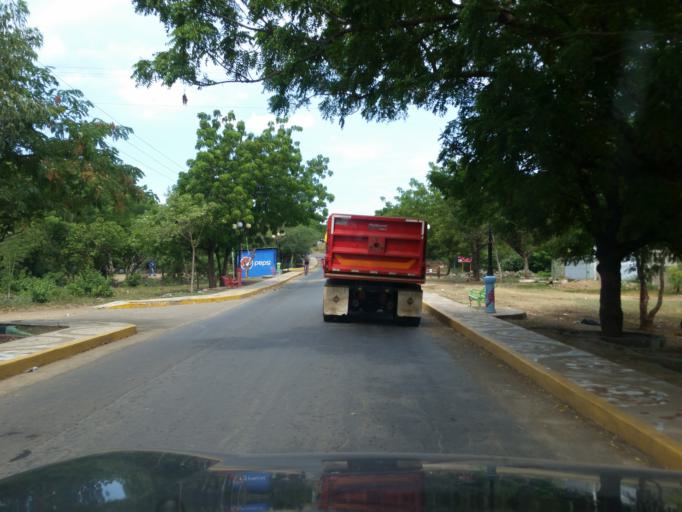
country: NI
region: Managua
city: Masachapa
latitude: 11.8127
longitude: -86.4871
